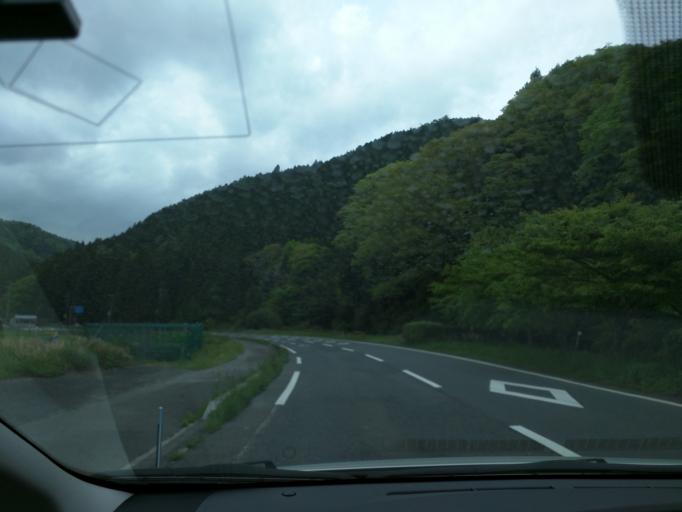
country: JP
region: Shiga Prefecture
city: Kusatsu
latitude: 34.8580
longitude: 135.9721
